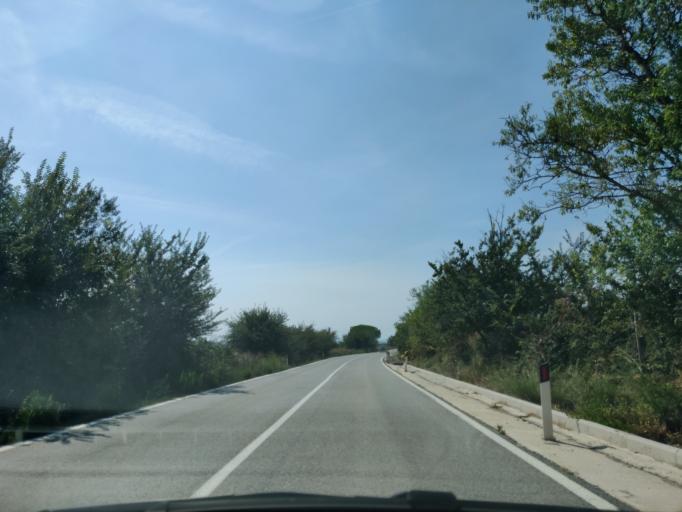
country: IT
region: Latium
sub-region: Provincia di Viterbo
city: Tarquinia
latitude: 42.2273
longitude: 11.7971
